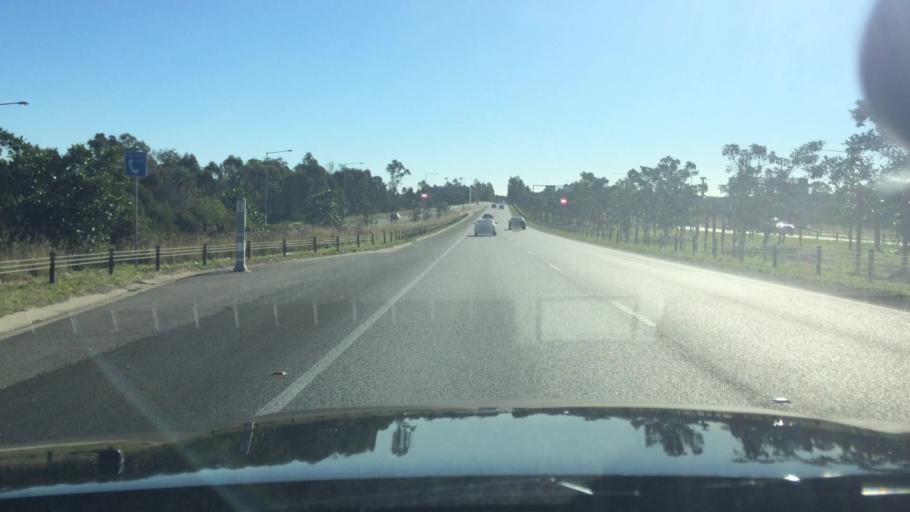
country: AU
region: New South Wales
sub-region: Blacktown
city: Doonside
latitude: -33.7941
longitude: 150.8550
